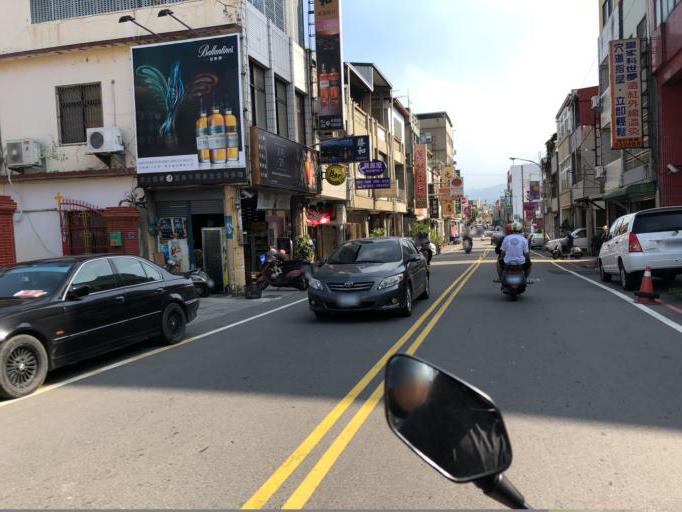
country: TW
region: Taiwan
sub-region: Miaoli
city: Miaoli
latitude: 24.5522
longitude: 120.8187
